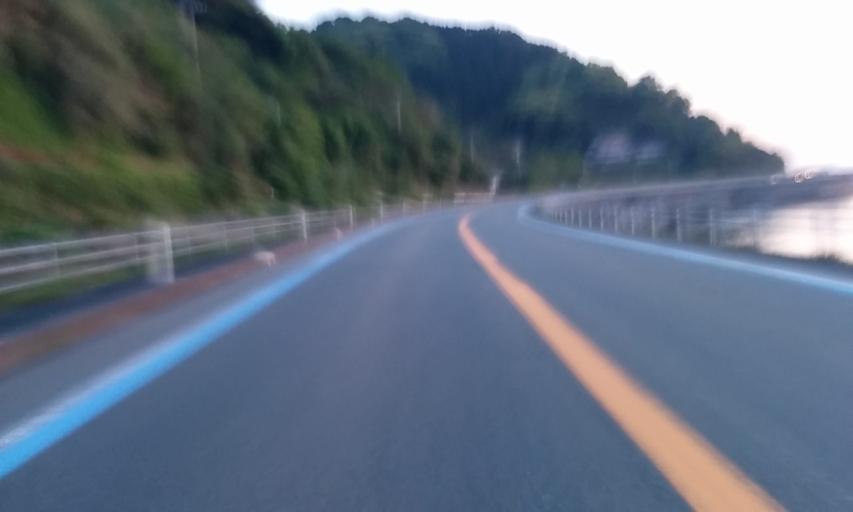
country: JP
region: Ehime
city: Ozu
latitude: 33.6300
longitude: 132.5175
